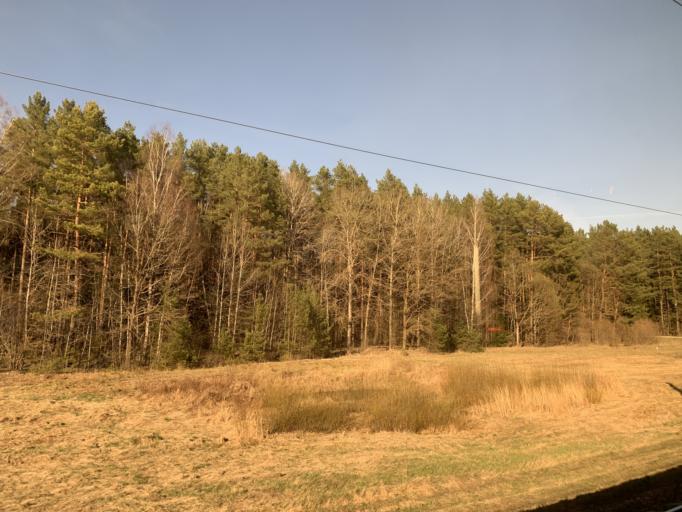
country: BY
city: Soly
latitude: 54.4911
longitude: 26.2937
